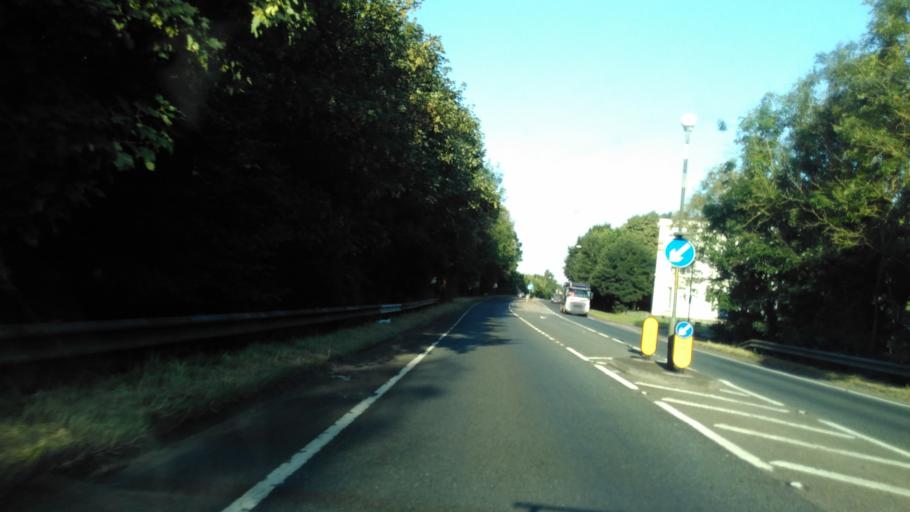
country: GB
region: England
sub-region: Kent
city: Blean
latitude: 51.2838
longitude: 1.0515
